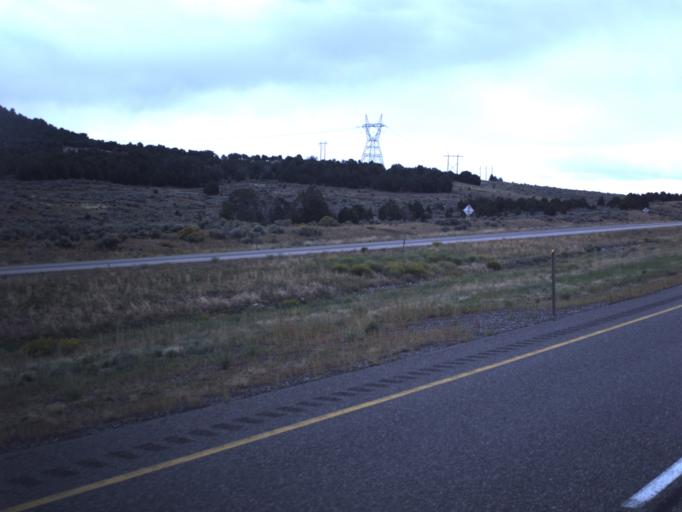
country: US
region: Utah
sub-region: Sevier County
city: Monroe
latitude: 38.5540
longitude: -112.4207
